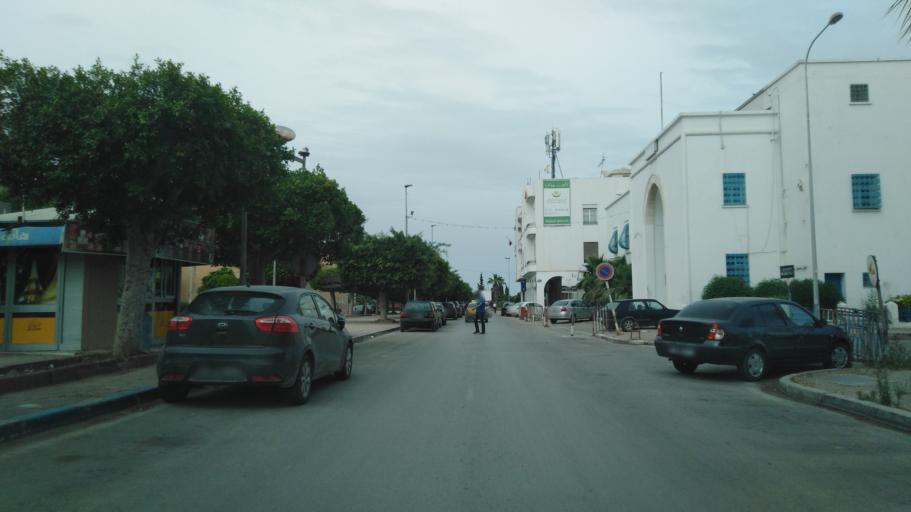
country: TN
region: Safaqis
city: Sfax
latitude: 34.7347
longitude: 10.7635
